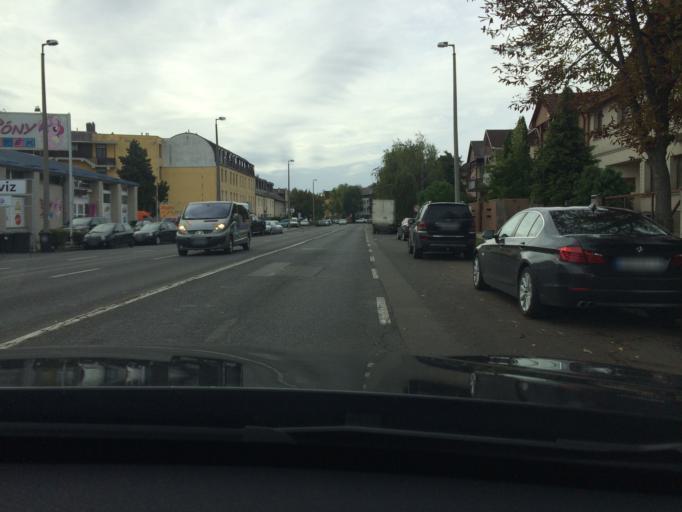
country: HU
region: Szabolcs-Szatmar-Bereg
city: Nyiregyhaza
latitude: 47.9626
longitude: 21.7240
